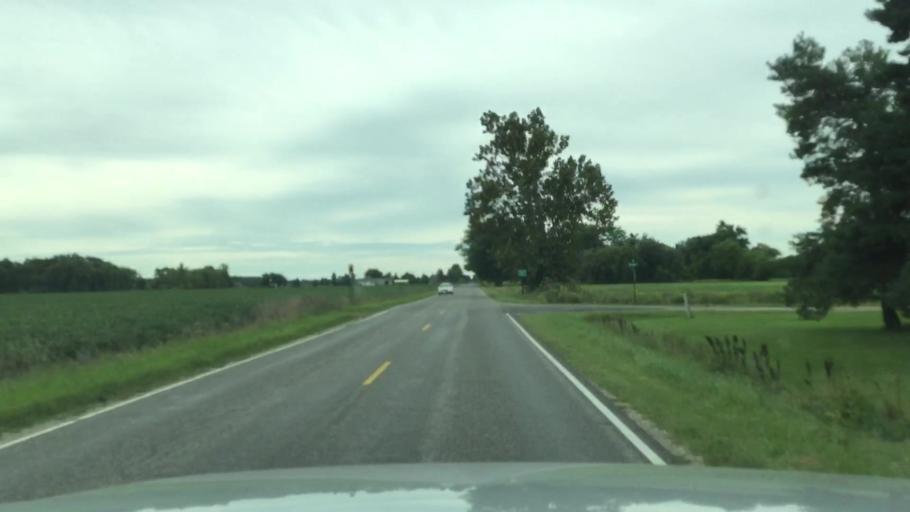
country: US
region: Michigan
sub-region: Shiawassee County
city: Durand
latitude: 43.0446
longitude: -83.9873
